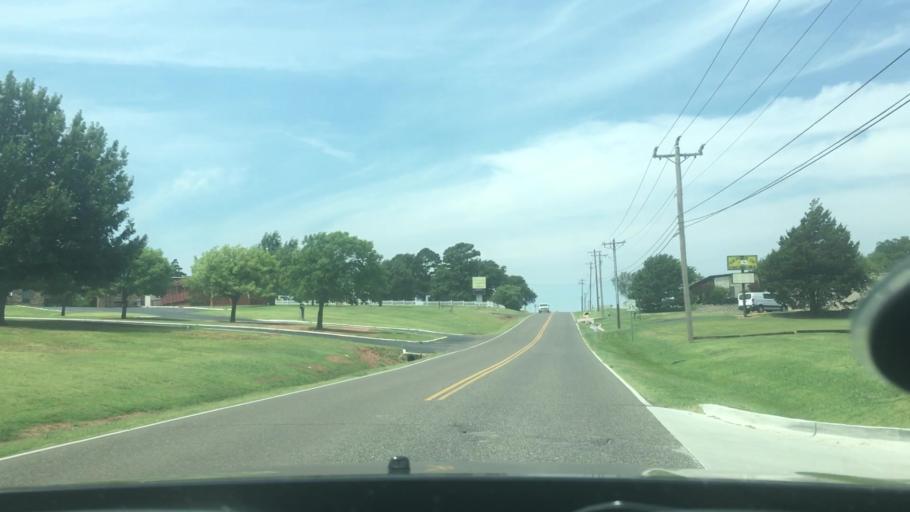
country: US
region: Oklahoma
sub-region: Pottawatomie County
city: Shawnee
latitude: 35.3617
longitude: -96.9075
